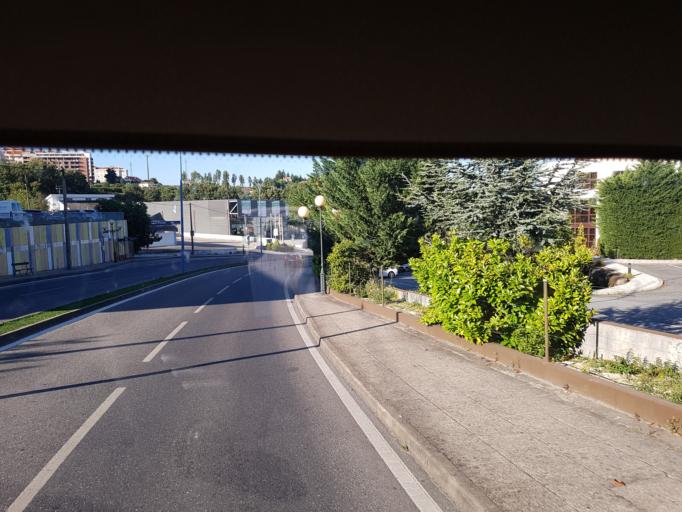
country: PT
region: Castelo Branco
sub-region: Covilha
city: Covilha
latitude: 40.2672
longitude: -7.4996
